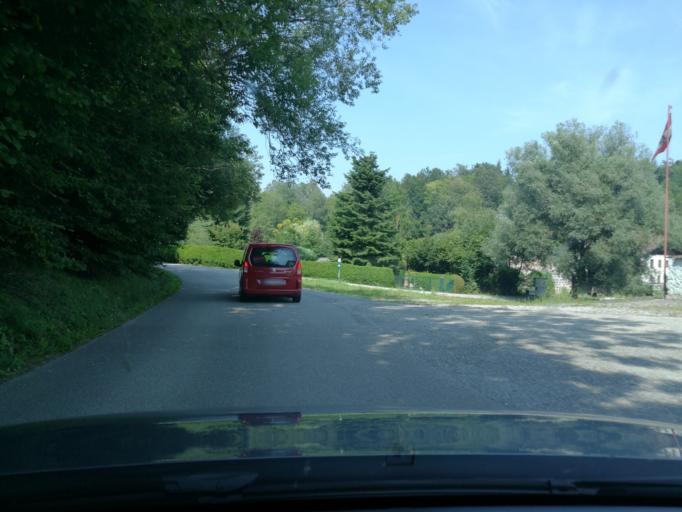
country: DE
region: Bavaria
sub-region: Lower Bavaria
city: Obernzell
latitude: 48.3715
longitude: 13.6570
